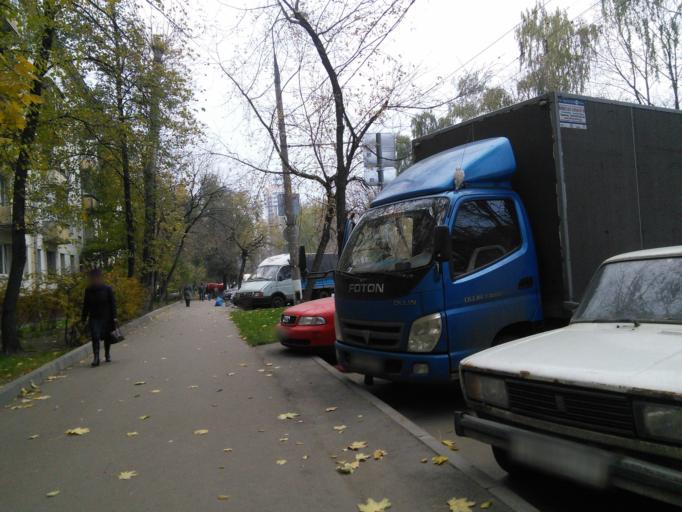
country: RU
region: Moskovskaya
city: Khoroshevo-Mnevniki
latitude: 55.7812
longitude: 37.4620
